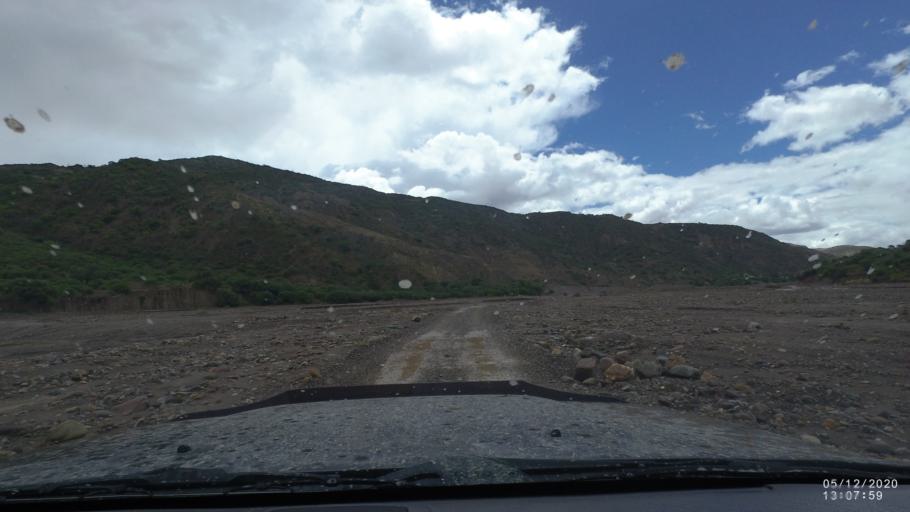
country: BO
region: Cochabamba
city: Sipe Sipe
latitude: -17.5610
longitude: -66.4502
